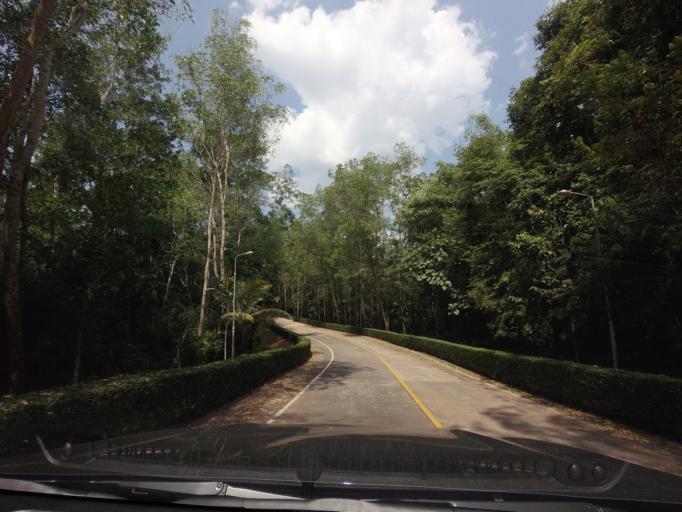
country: TH
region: Nan
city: Bo Kluea
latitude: 19.0222
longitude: 101.2077
